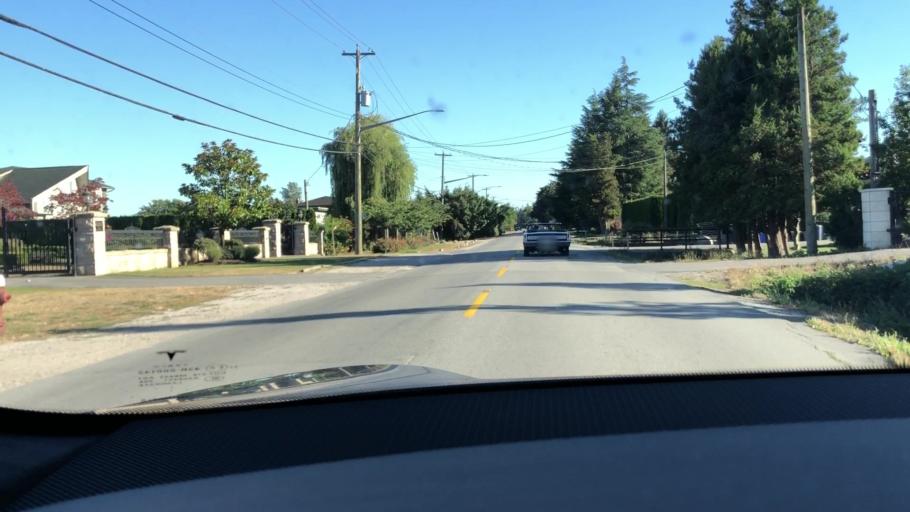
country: CA
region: British Columbia
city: Richmond
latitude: 49.1678
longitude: -123.0692
